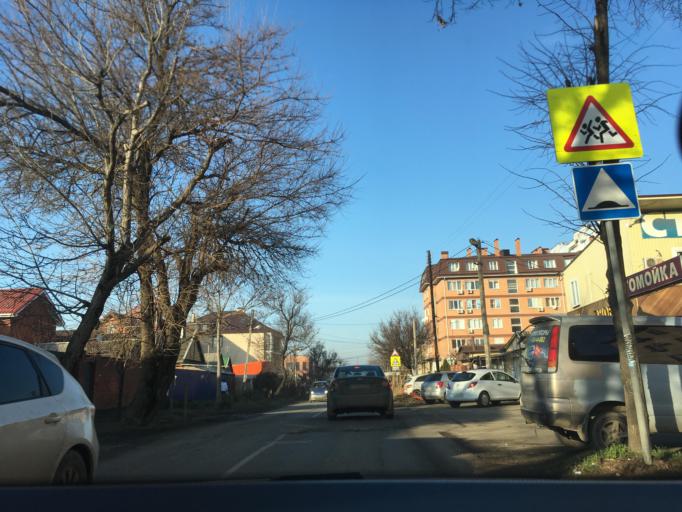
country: RU
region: Krasnodarskiy
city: Krasnodar
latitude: 45.0677
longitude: 39.0217
